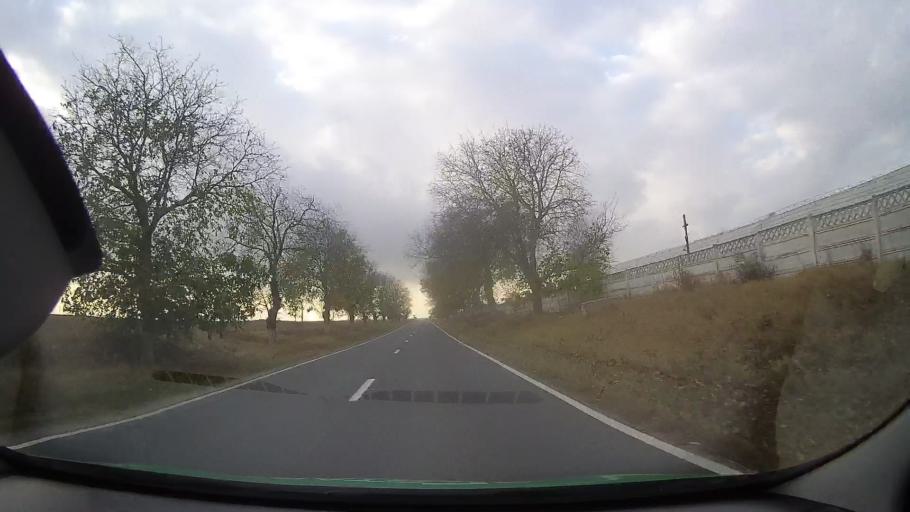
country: RO
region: Constanta
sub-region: Comuna Adamclisi
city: Adamclisi
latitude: 44.0882
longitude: 27.9696
